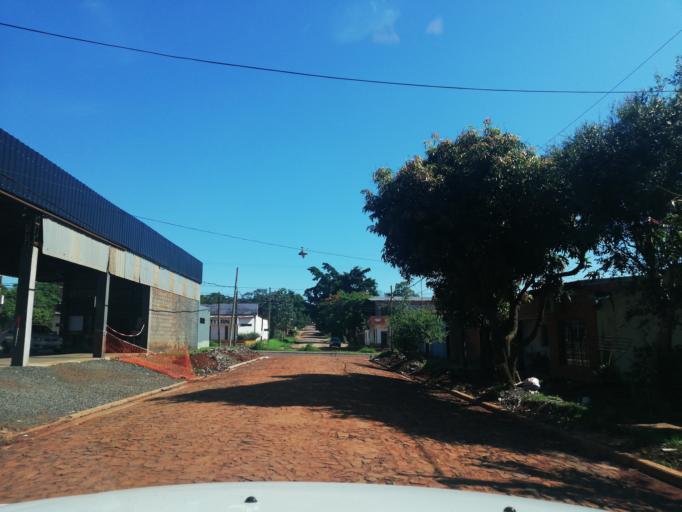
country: AR
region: Misiones
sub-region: Departamento de Capital
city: Posadas
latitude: -27.3982
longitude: -55.9227
